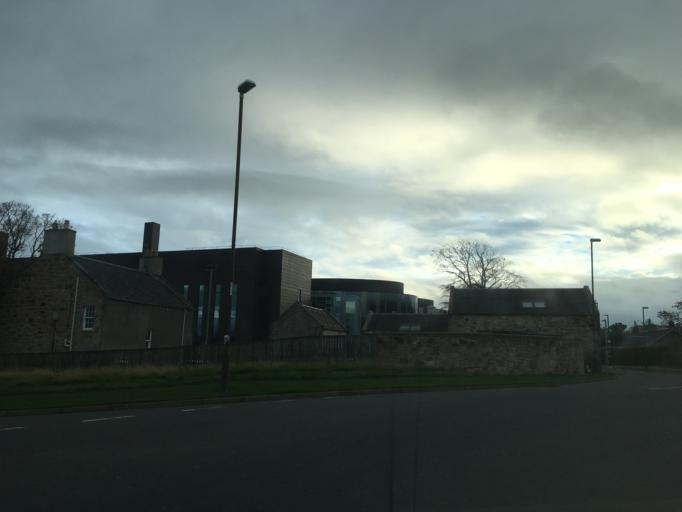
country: GB
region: Scotland
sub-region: Midlothian
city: Loanhead
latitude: 55.8669
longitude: -3.1987
